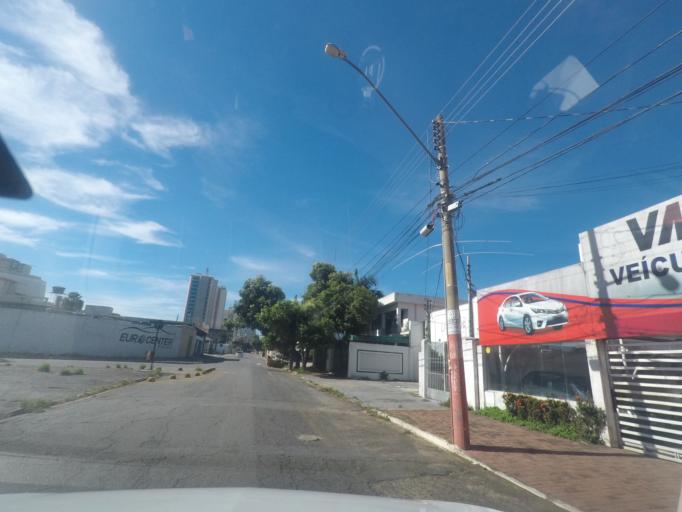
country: BR
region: Goias
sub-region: Goiania
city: Goiania
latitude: -16.6739
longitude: -49.2666
